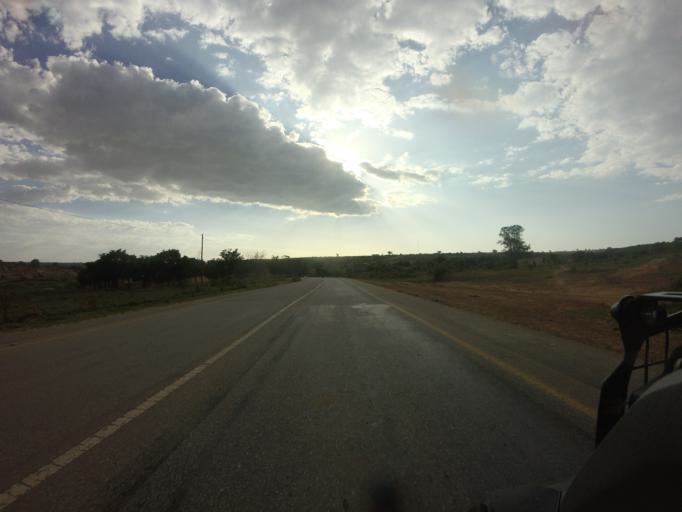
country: AO
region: Huila
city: Lubango
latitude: -14.6641
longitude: 13.9005
